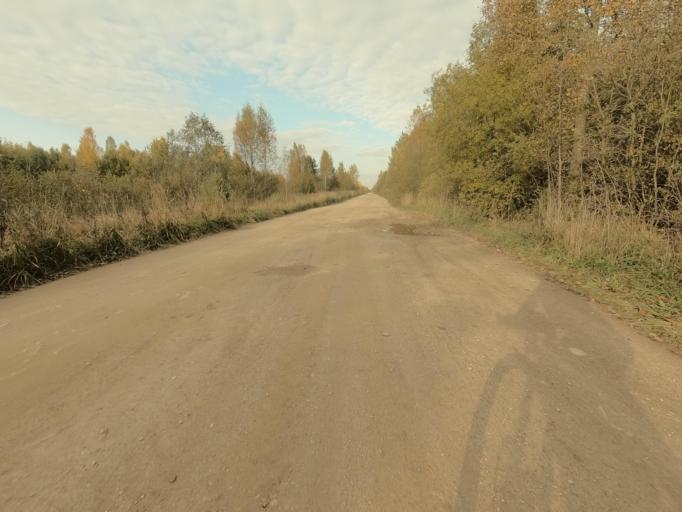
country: RU
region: Novgorod
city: Volkhovskiy
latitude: 58.9056
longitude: 31.0363
